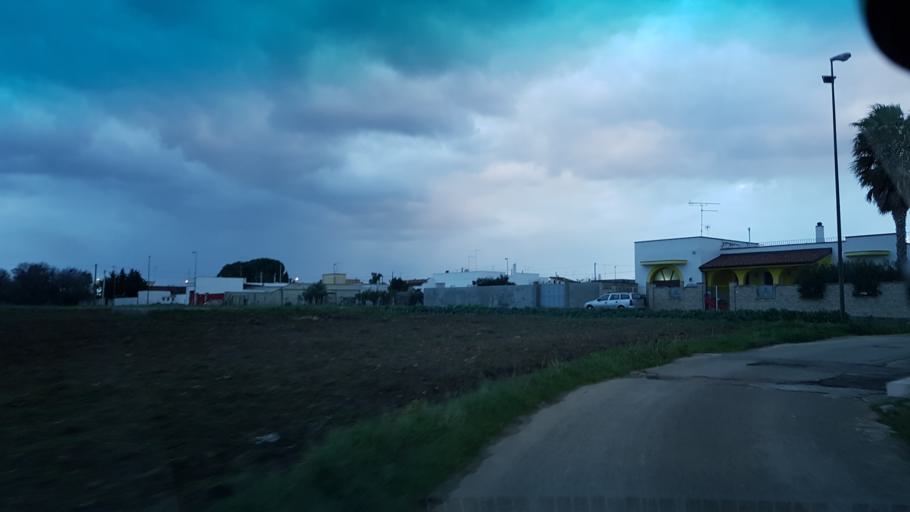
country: IT
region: Apulia
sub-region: Provincia di Brindisi
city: Torchiarolo
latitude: 40.4895
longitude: 18.0557
